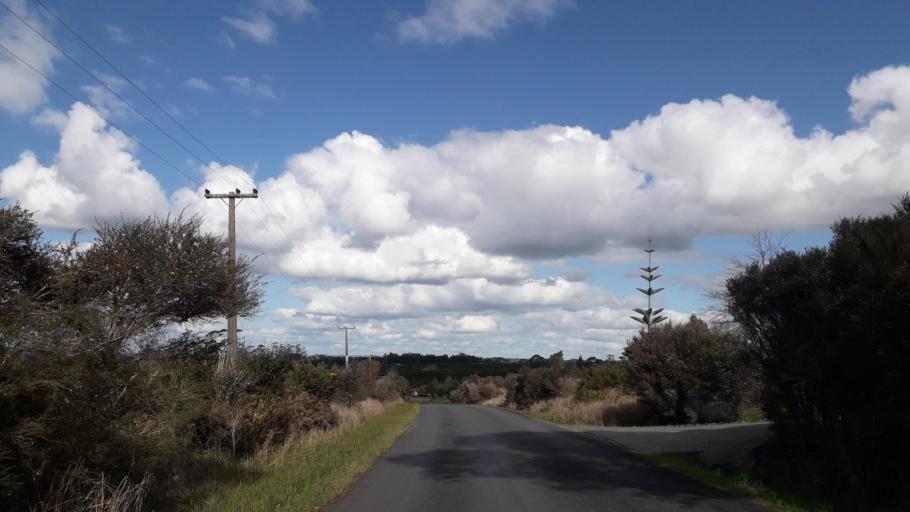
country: NZ
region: Northland
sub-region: Far North District
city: Kerikeri
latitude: -35.1826
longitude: 173.9360
